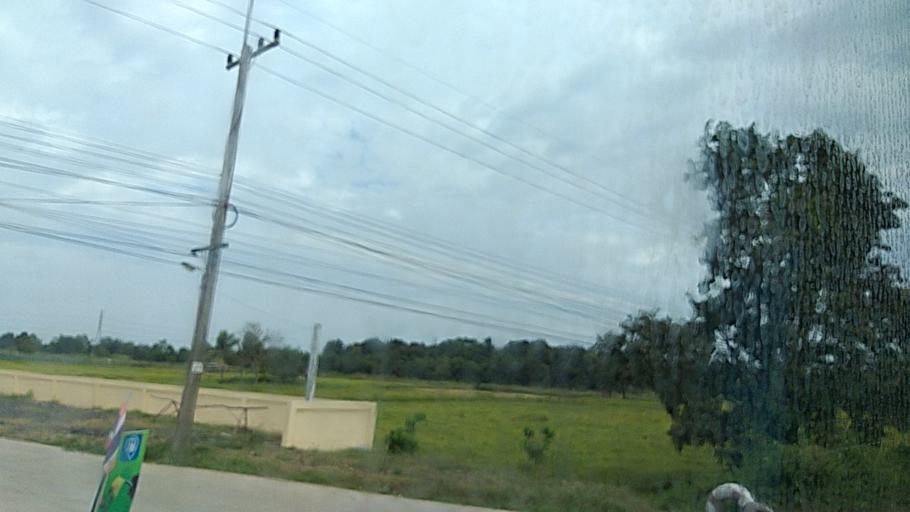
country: TH
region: Kalasin
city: Khong Chai
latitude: 16.1348
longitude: 103.4500
